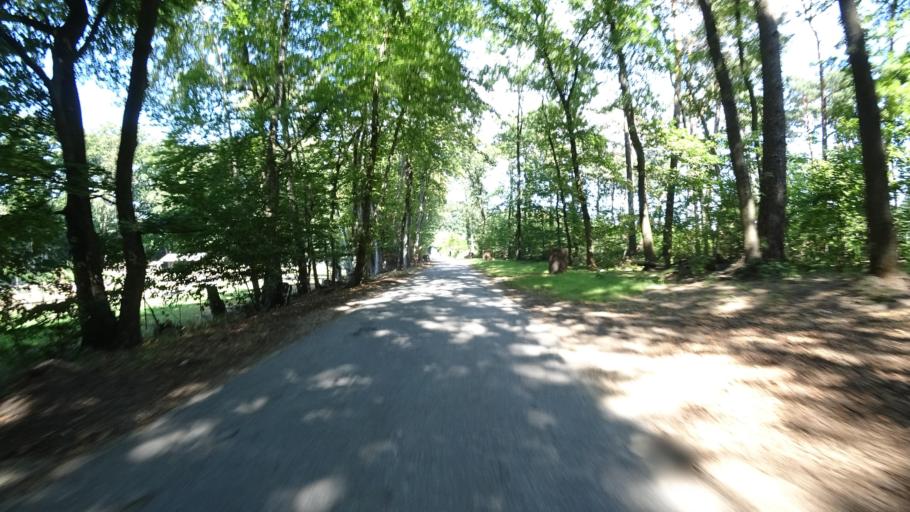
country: DE
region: North Rhine-Westphalia
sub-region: Regierungsbezirk Detmold
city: Steinhagen
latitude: 51.9508
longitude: 8.4585
